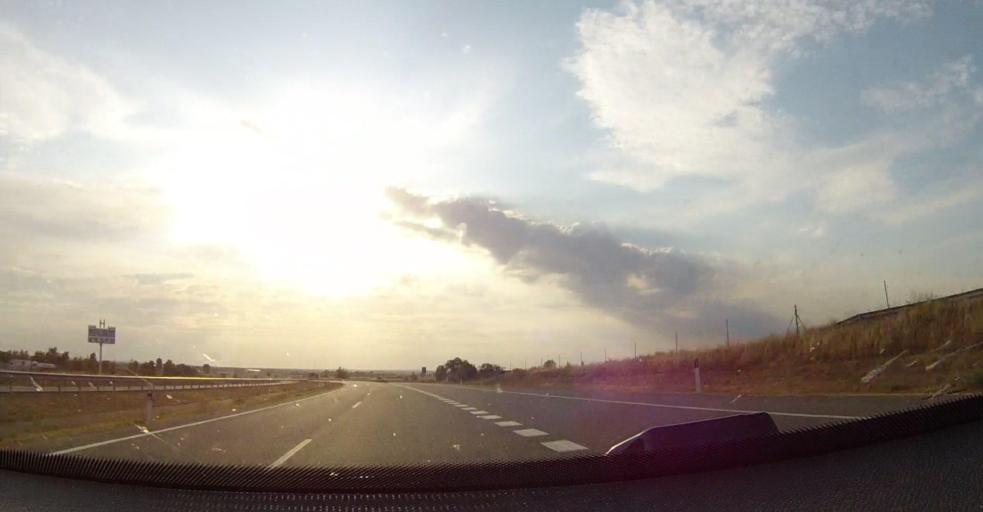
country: ES
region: Castille and Leon
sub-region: Provincia de Burgos
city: Sasamon
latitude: 42.4009
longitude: -4.0339
